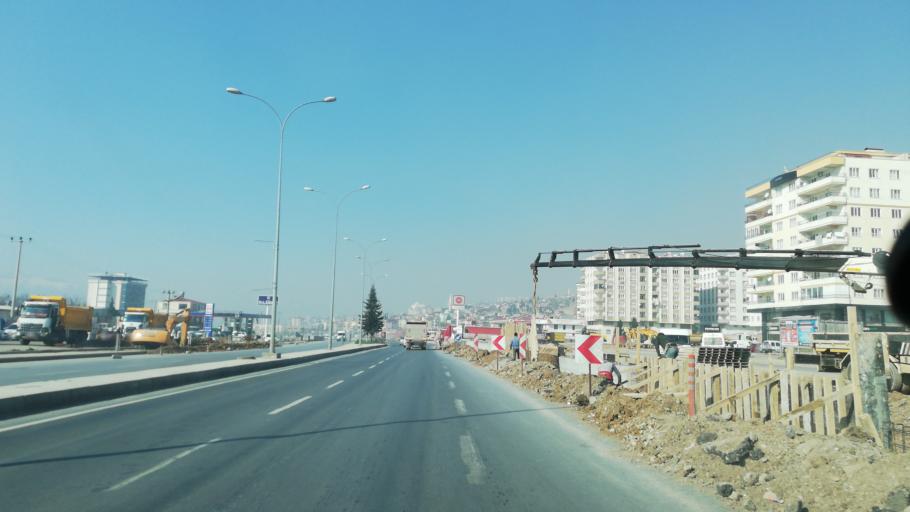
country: TR
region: Kahramanmaras
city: Kahramanmaras
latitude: 37.5694
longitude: 36.9205
